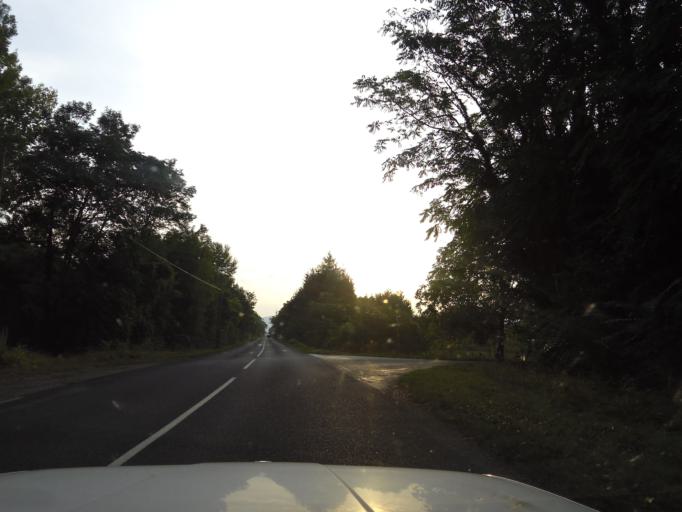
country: FR
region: Rhone-Alpes
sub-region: Departement de l'Ain
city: Saint-Jean-de-Niost
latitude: 45.8132
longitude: 5.2178
